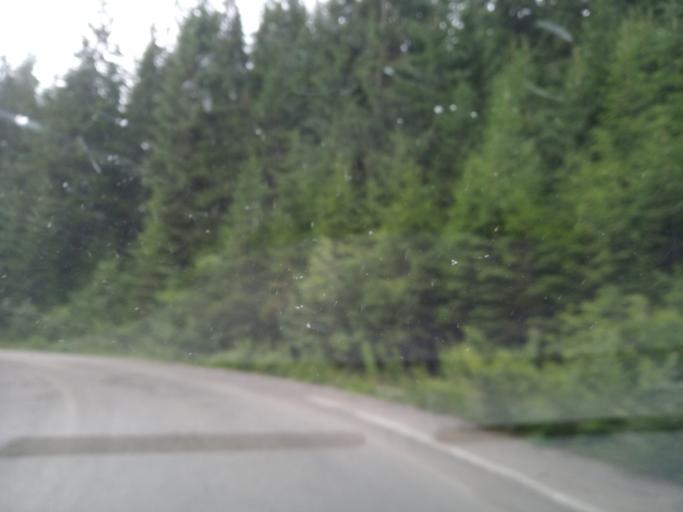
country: RO
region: Valcea
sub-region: Comuna Voineasa
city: Voineasa
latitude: 45.4158
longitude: 23.7194
